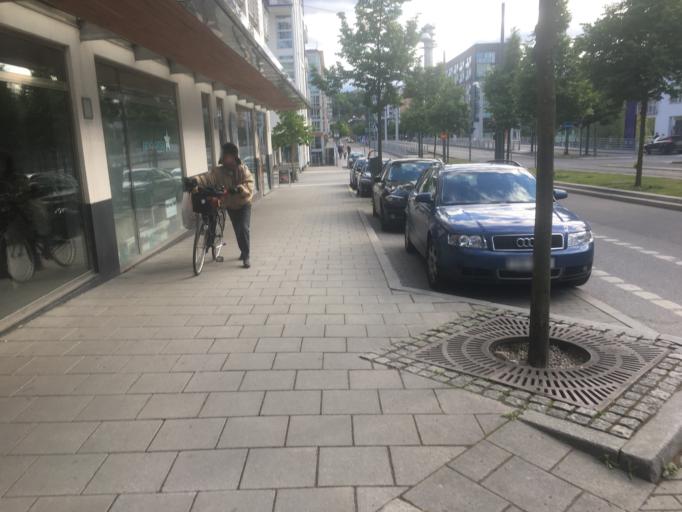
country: SE
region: Stockholm
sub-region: Stockholms Kommun
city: OEstermalm
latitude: 59.3048
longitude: 18.1064
